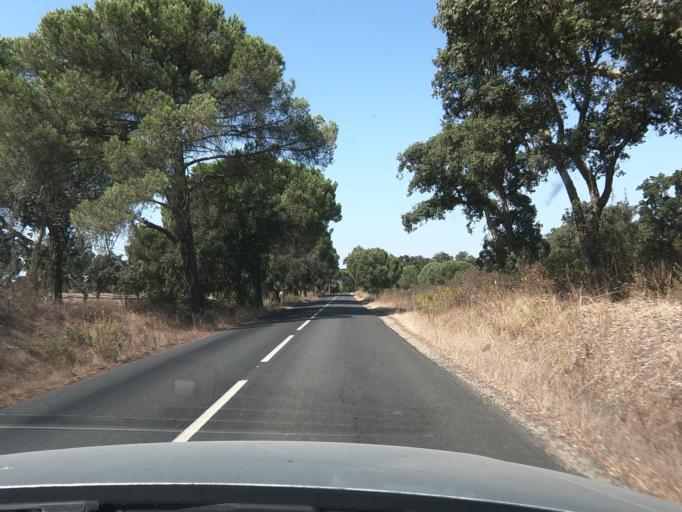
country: PT
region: Setubal
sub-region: Alcacer do Sal
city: Alcacer do Sal
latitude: 38.3399
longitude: -8.4451
